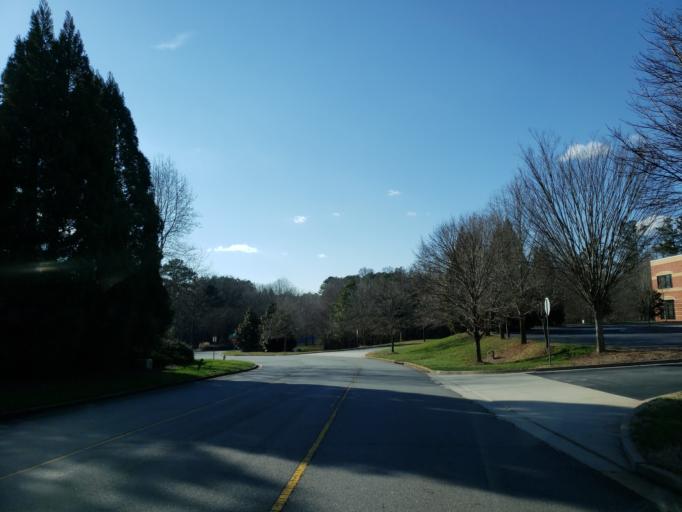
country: US
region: Georgia
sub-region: Cobb County
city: Marietta
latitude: 33.9858
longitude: -84.5174
